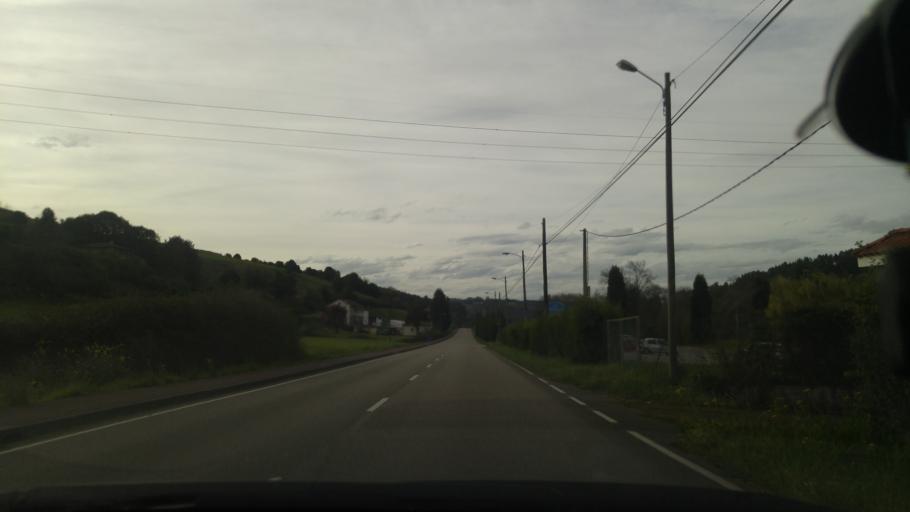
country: ES
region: Asturias
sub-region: Province of Asturias
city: Corvera de Asturias
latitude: 43.4932
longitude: -5.8519
